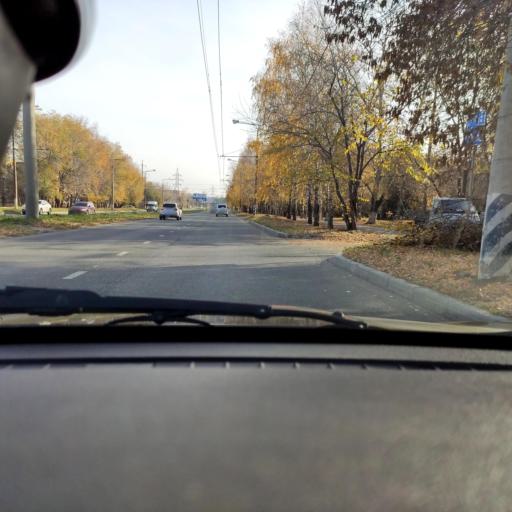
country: RU
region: Samara
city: Tol'yatti
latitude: 53.5140
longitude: 49.4459
